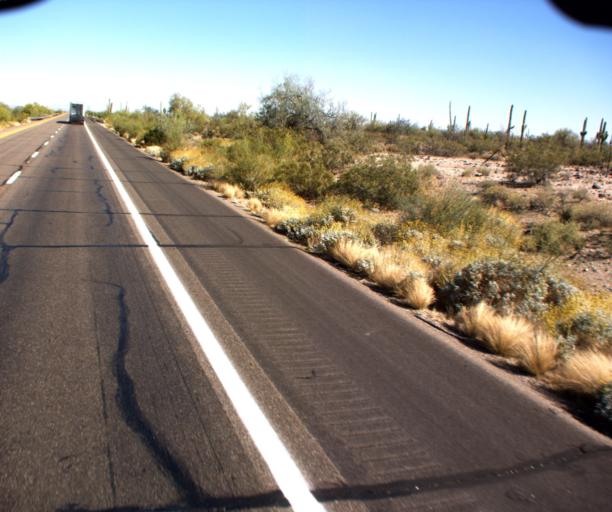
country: US
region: Arizona
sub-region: Pinal County
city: Maricopa
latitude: 32.8315
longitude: -112.0625
